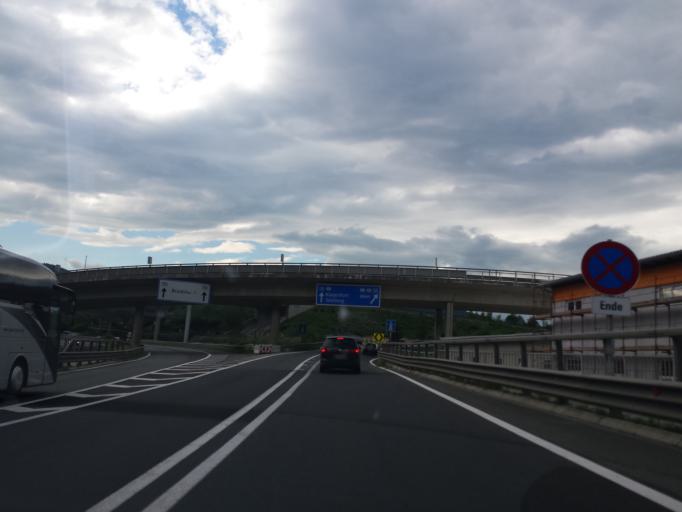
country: AT
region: Styria
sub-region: Politischer Bezirk Bruck-Muerzzuschlag
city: Bruck an der Mur
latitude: 47.4053
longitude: 15.2843
